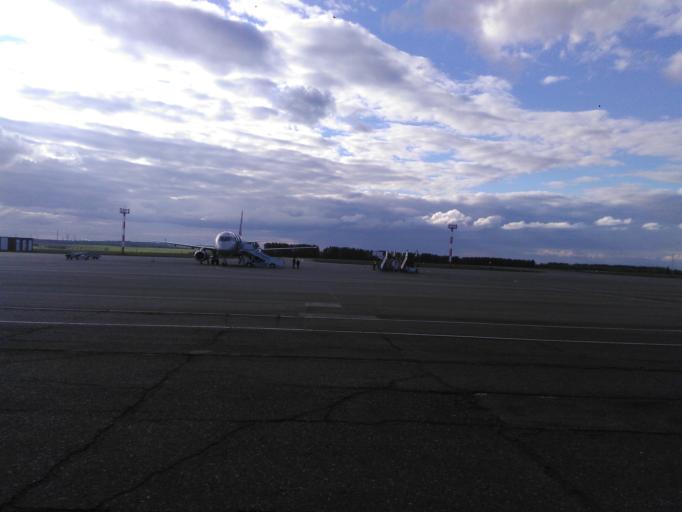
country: RU
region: Tatarstan
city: Yelabuga
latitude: 55.5648
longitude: 52.1016
